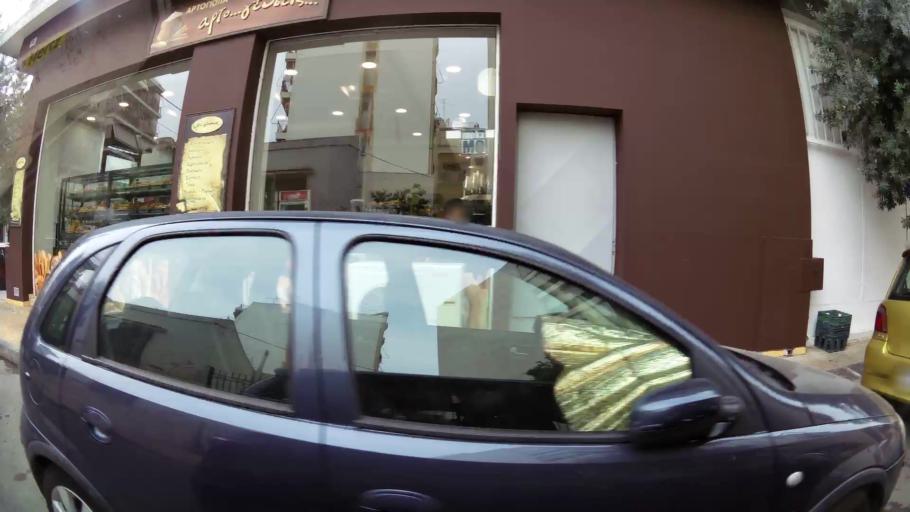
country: GR
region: Attica
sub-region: Nomarchia Athinas
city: Nea Filadelfeia
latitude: 38.0371
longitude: 23.7463
